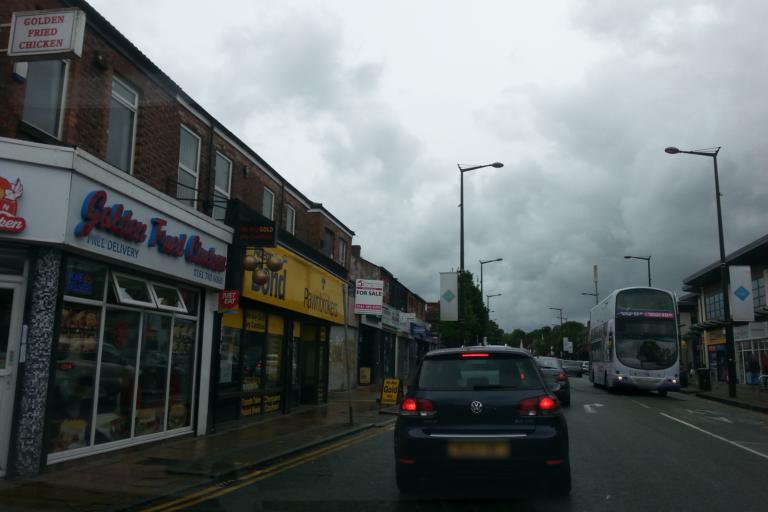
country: GB
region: England
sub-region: Manchester
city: Crumpsall
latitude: 53.5122
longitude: -2.2453
